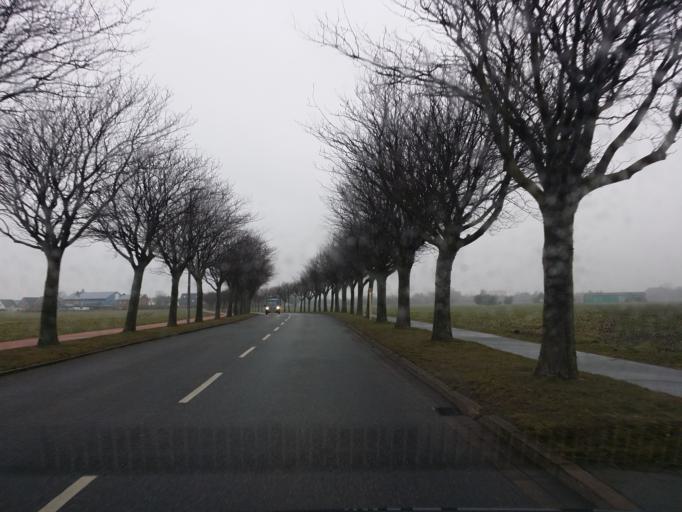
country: DE
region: Schleswig-Holstein
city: Burg auf Fehmarn
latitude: 54.4252
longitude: 11.2052
